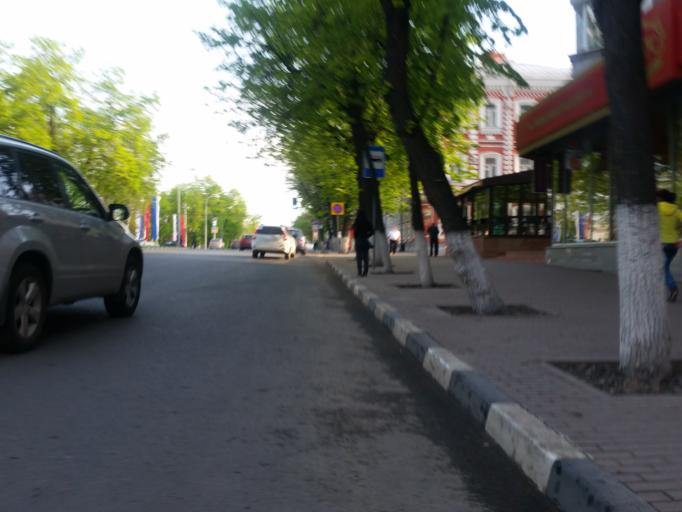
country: RU
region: Ulyanovsk
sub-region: Ulyanovskiy Rayon
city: Ulyanovsk
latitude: 54.3138
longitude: 48.3962
